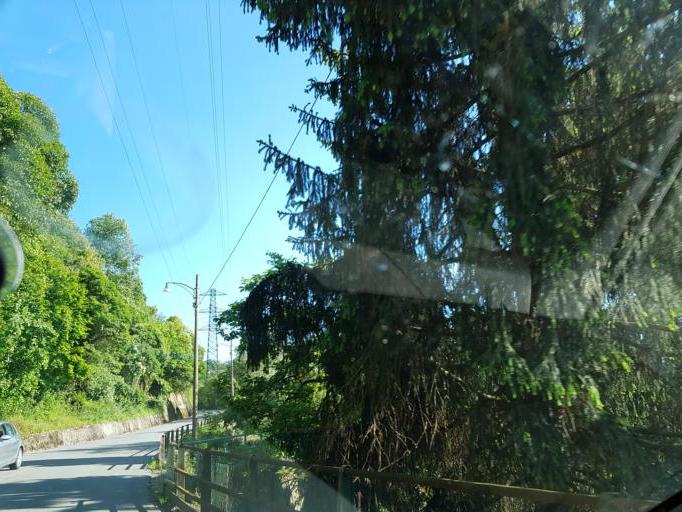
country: IT
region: Liguria
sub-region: Provincia di Genova
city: Manesseno
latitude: 44.4734
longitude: 8.9163
